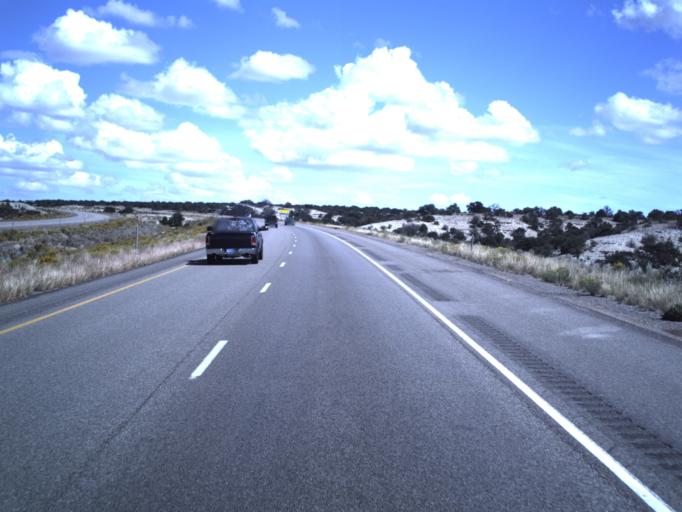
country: US
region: Utah
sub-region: Emery County
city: Ferron
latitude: 38.8412
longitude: -110.9590
